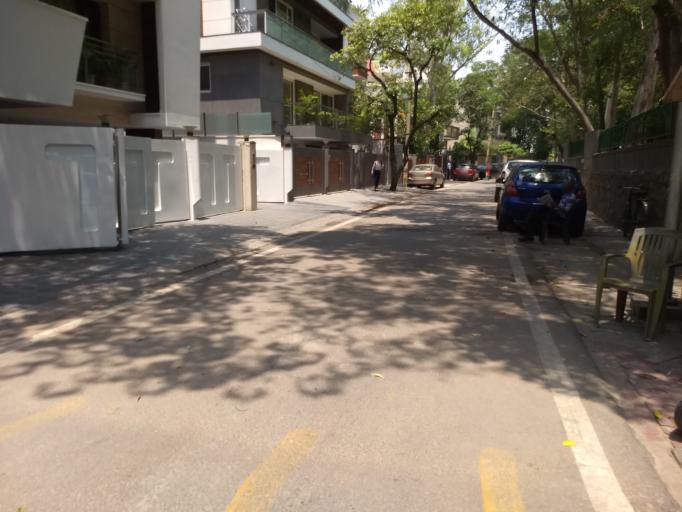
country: IN
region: NCT
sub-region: New Delhi
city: New Delhi
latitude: 28.5309
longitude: 77.2009
